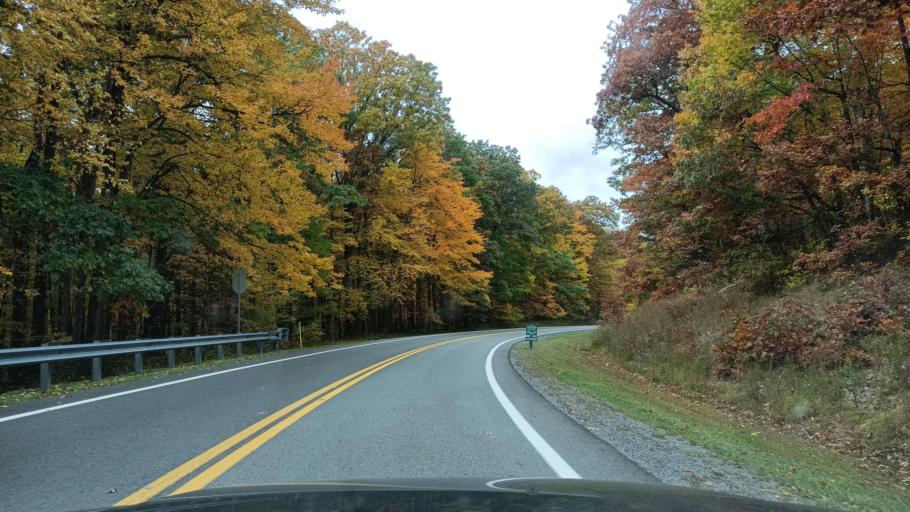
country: US
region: West Virginia
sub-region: Monongalia County
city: Cheat Lake
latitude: 39.6568
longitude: -79.7816
